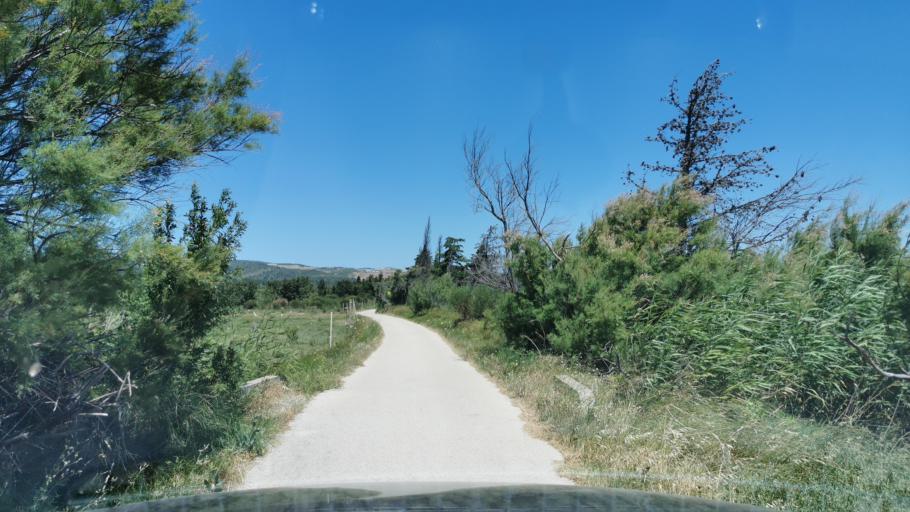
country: FR
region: Languedoc-Roussillon
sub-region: Departement de l'Aude
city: Peyriac-de-Mer
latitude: 43.1014
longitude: 2.9598
